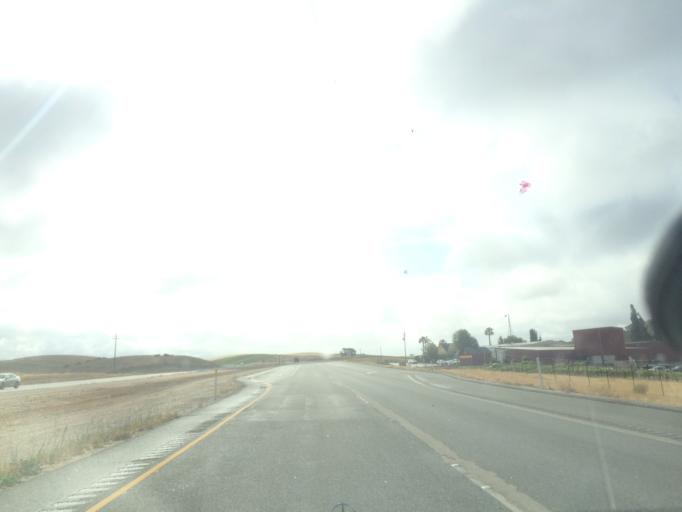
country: US
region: California
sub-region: San Luis Obispo County
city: Paso Robles
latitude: 35.6564
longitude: -120.5372
